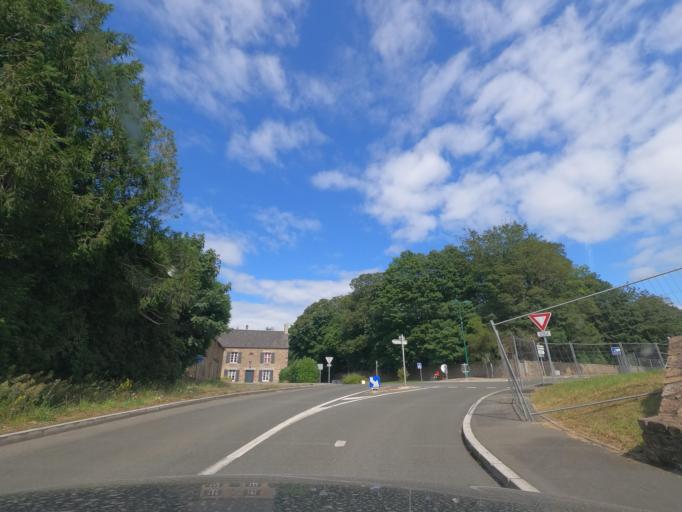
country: FR
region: Pays de la Loire
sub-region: Departement de la Mayenne
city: Landivy
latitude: 48.4784
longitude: -1.0369
